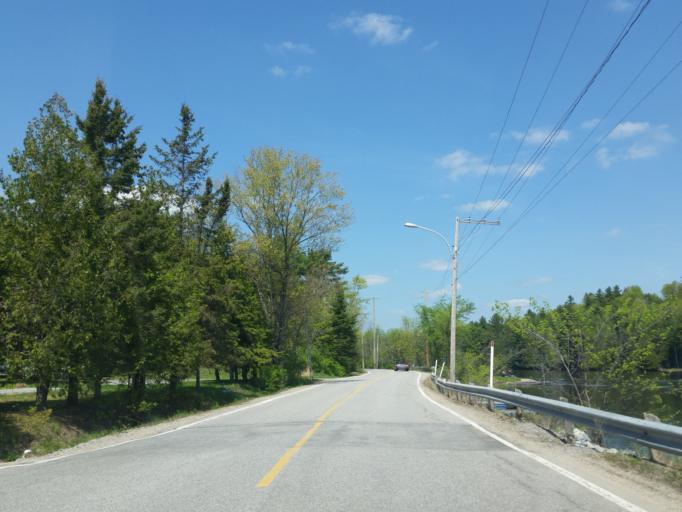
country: CA
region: Quebec
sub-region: Outaouais
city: Wakefield
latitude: 45.6039
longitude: -75.8898
